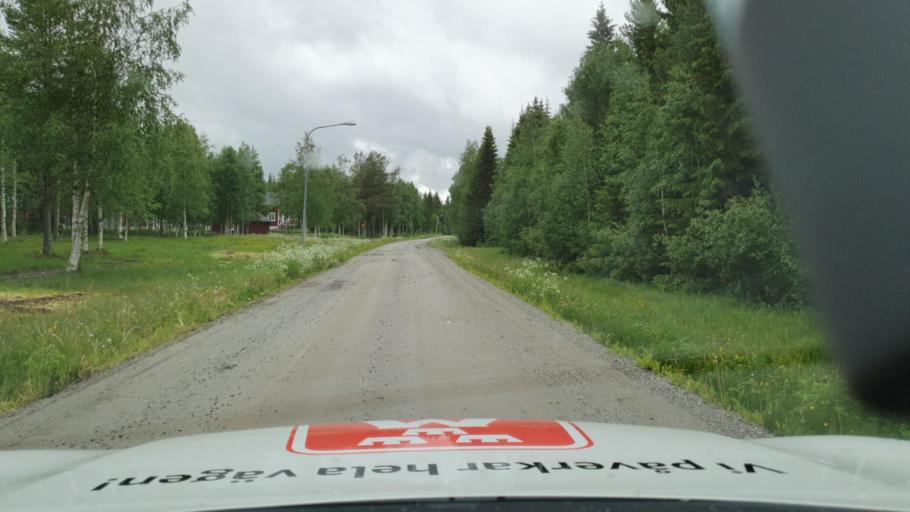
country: SE
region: Vaesterbotten
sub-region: Dorotea Kommun
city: Dorotea
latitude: 64.0936
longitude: 16.6575
